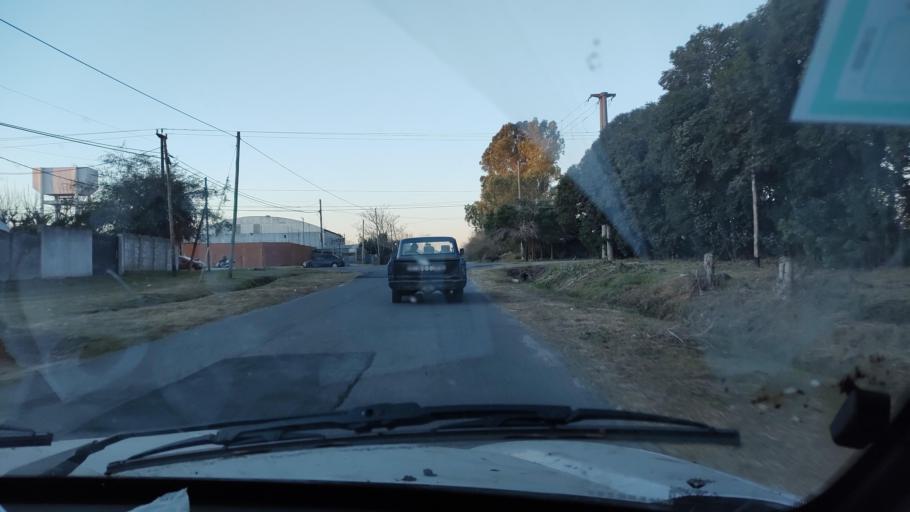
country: AR
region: Buenos Aires
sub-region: Partido de La Plata
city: La Plata
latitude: -34.9083
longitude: -58.0143
